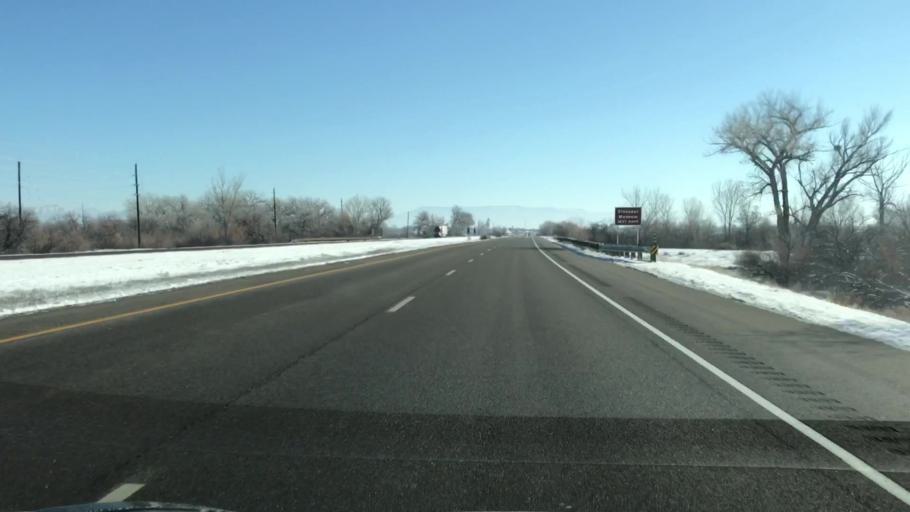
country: US
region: Colorado
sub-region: Mesa County
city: Fruita
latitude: 39.1598
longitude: -108.7585
